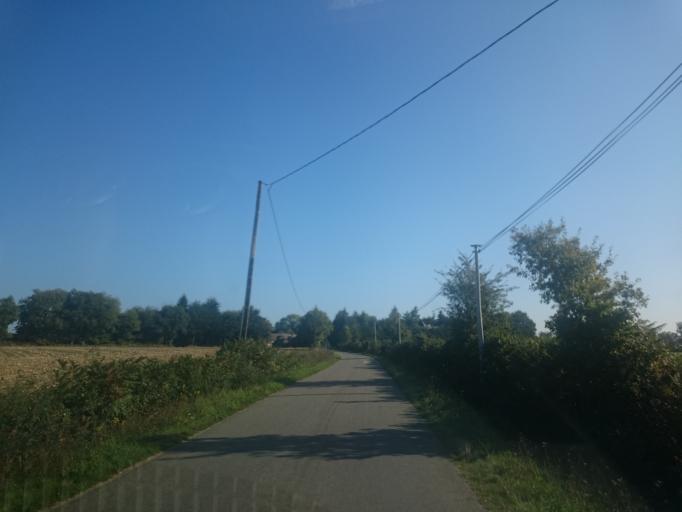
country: FR
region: Brittany
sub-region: Departement d'Ille-et-Vilaine
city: Tresboeuf
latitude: 47.9193
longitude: -1.5698
